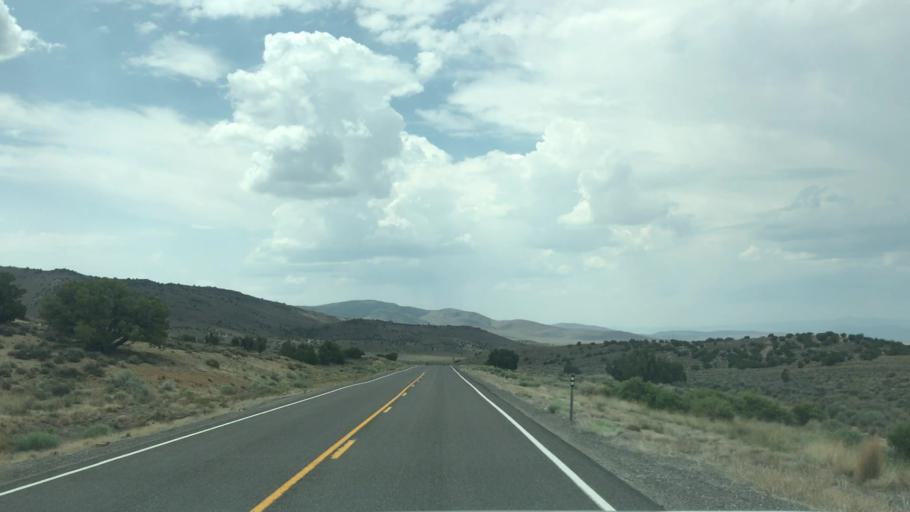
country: US
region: Nevada
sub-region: Eureka County
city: Eureka
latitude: 39.4061
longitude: -115.6997
